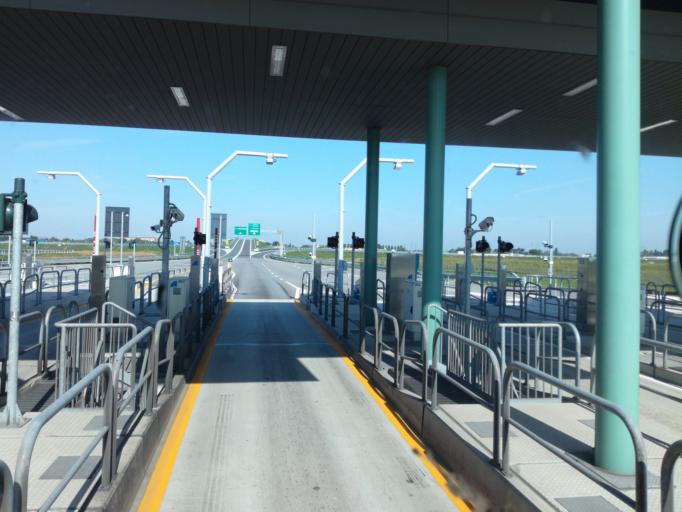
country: IT
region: Lombardy
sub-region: Provincia di Lodi
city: Sordio
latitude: 45.3474
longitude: 9.3552
